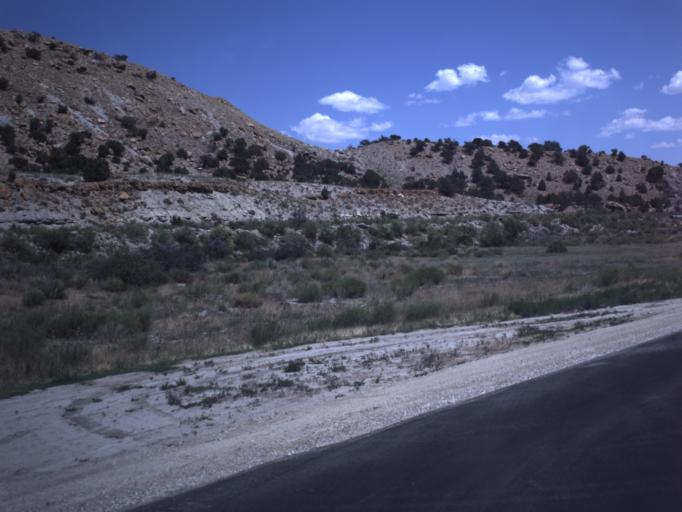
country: US
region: Utah
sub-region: Emery County
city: Orangeville
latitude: 39.2684
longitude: -111.1424
